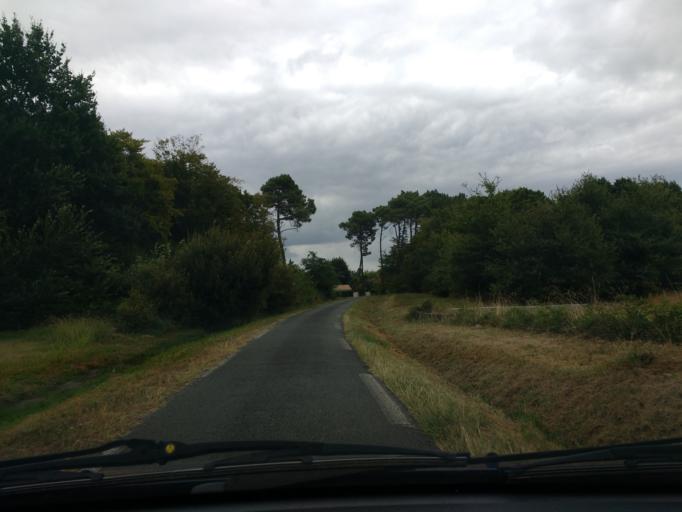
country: FR
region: Aquitaine
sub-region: Departement de la Gironde
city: Gradignan
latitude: 44.7784
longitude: -0.6247
